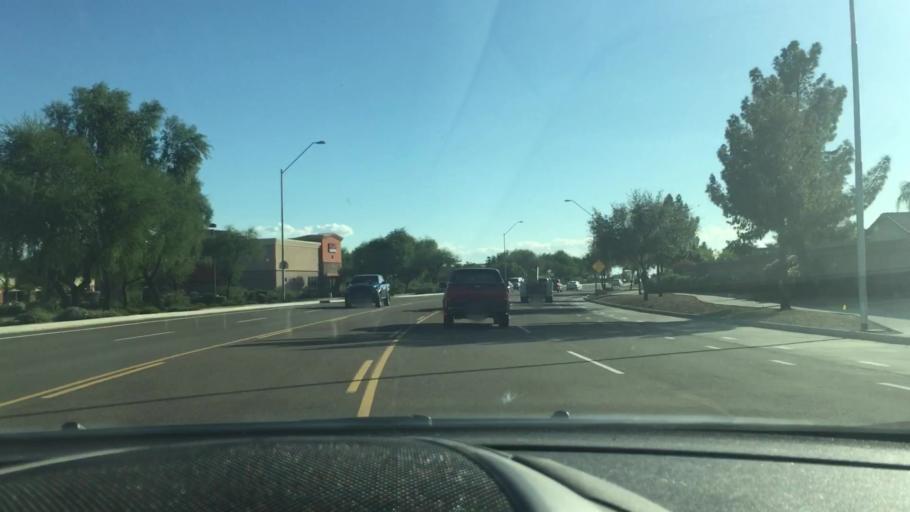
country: US
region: Arizona
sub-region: Maricopa County
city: Sun City
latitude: 33.6744
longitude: -112.2381
